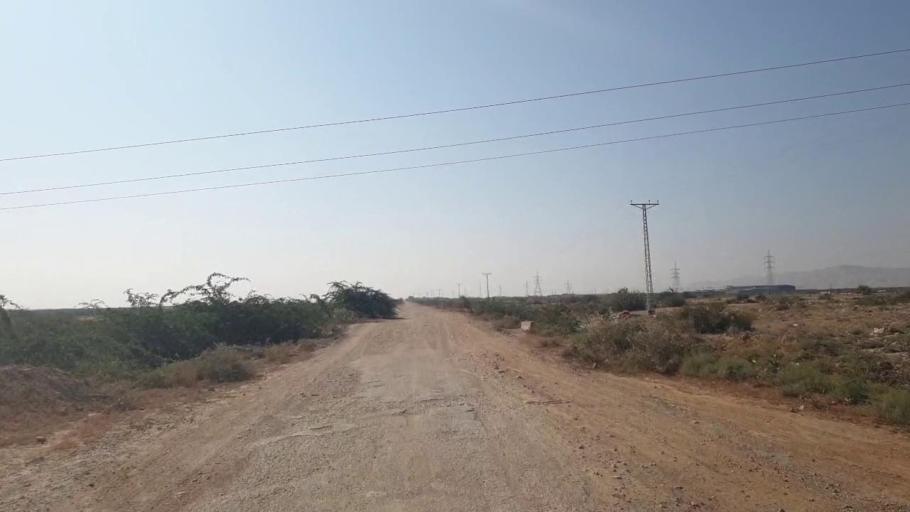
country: PK
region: Sindh
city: Gharo
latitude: 25.1635
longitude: 67.7282
